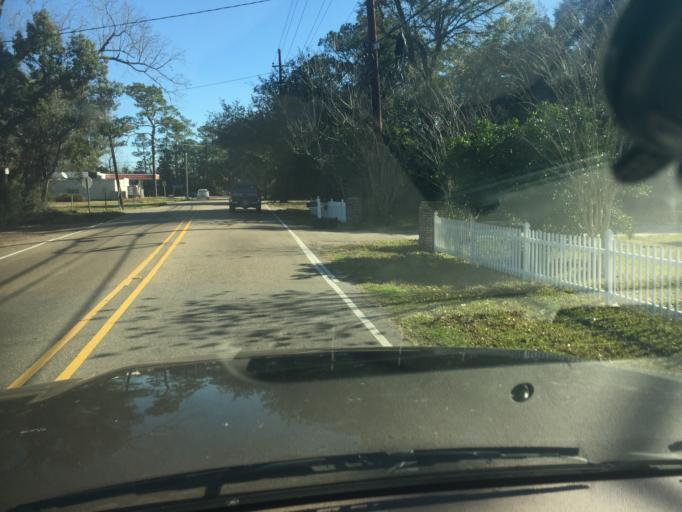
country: US
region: Louisiana
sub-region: Saint Tammany Parish
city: Slidell
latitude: 30.3104
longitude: -89.7325
